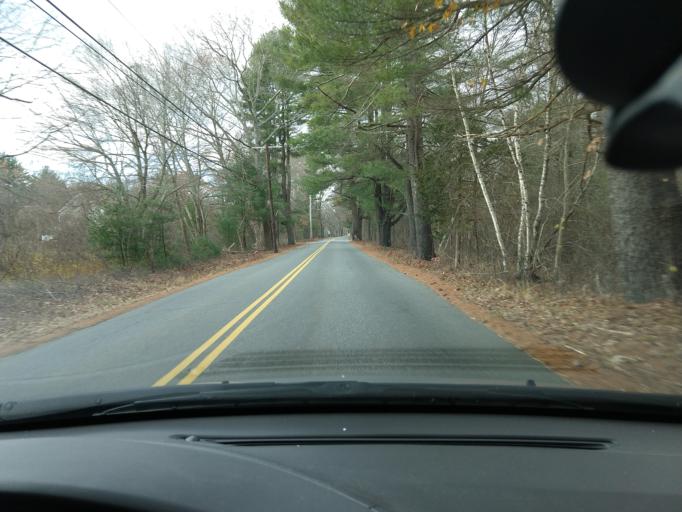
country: US
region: Massachusetts
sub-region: Middlesex County
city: Sudbury
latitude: 42.3973
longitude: -71.3830
